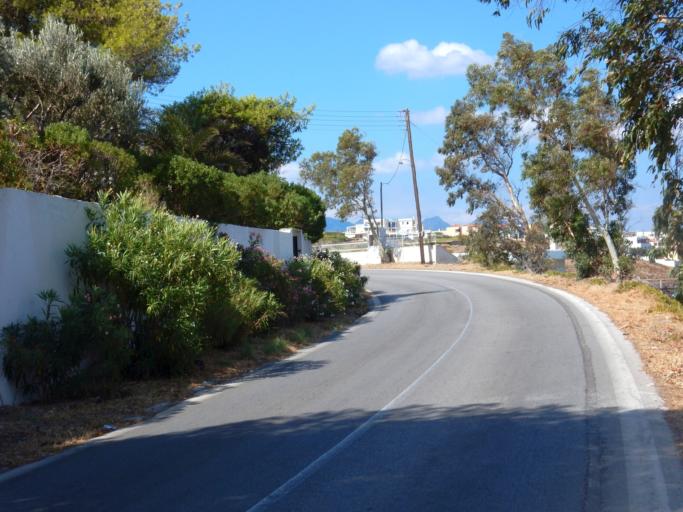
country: GR
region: Attica
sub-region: Nomos Piraios
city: Aegina
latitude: 37.6970
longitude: 23.4642
